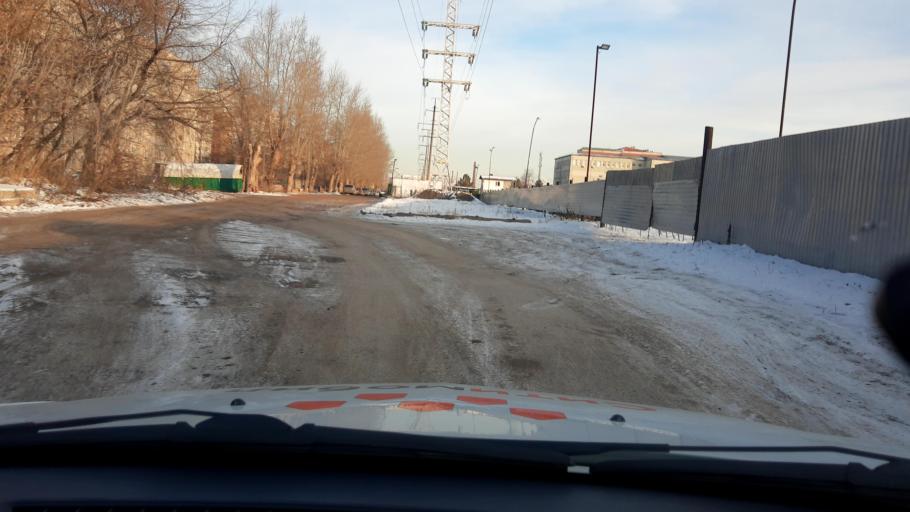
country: RU
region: Bashkortostan
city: Ufa
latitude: 54.7909
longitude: 56.0547
